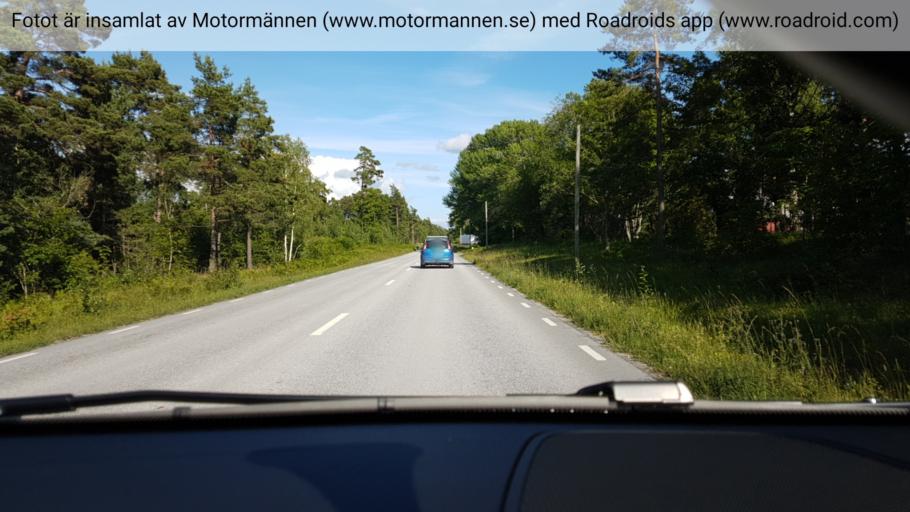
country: SE
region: Gotland
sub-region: Gotland
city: Slite
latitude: 57.7461
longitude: 18.6721
